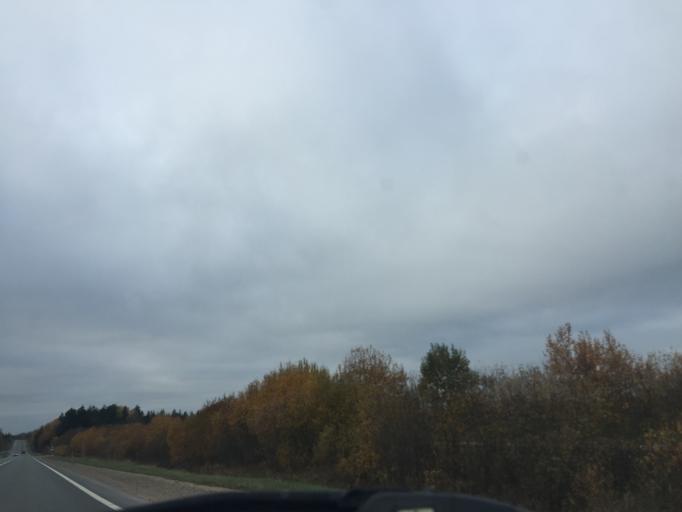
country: LV
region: Saldus Rajons
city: Saldus
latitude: 56.6723
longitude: 22.3715
